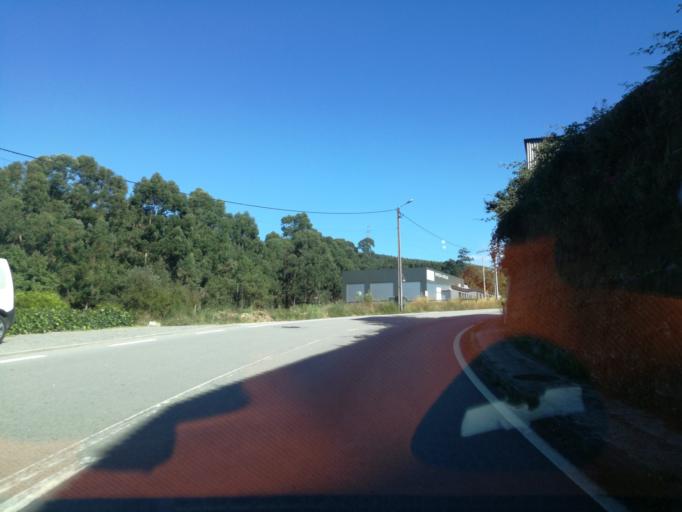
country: PT
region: Porto
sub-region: Pacos de Ferreira
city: Seroa
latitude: 41.2585
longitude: -8.4658
